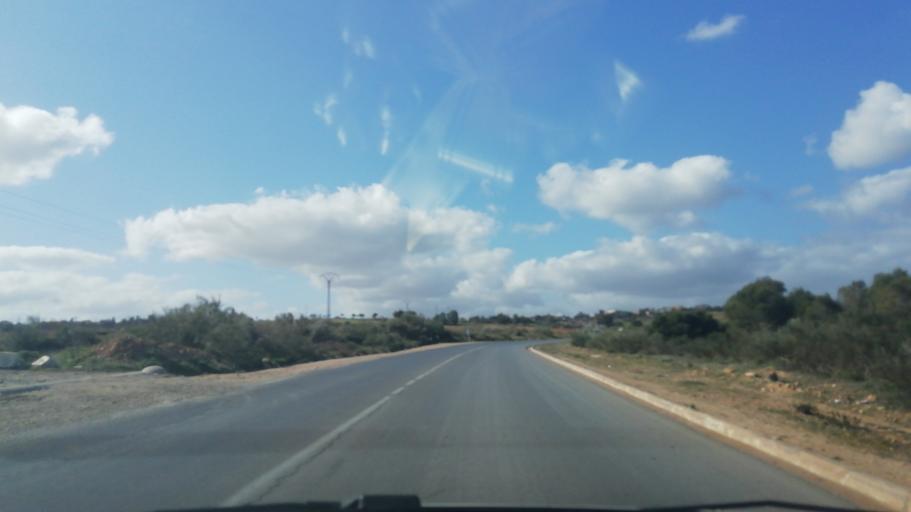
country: DZ
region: Relizane
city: Mazouna
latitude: 36.2926
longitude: 0.6554
